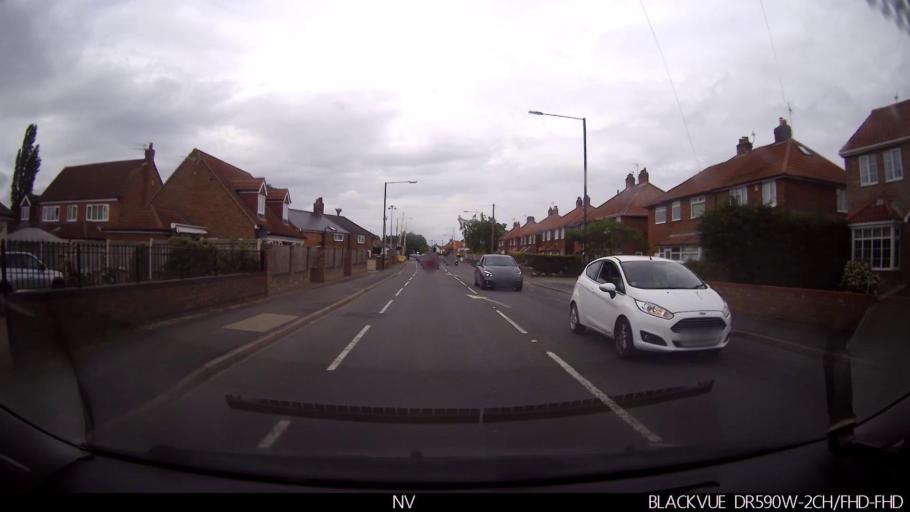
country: GB
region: England
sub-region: City of York
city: Haxby
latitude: 54.0034
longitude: -1.0733
